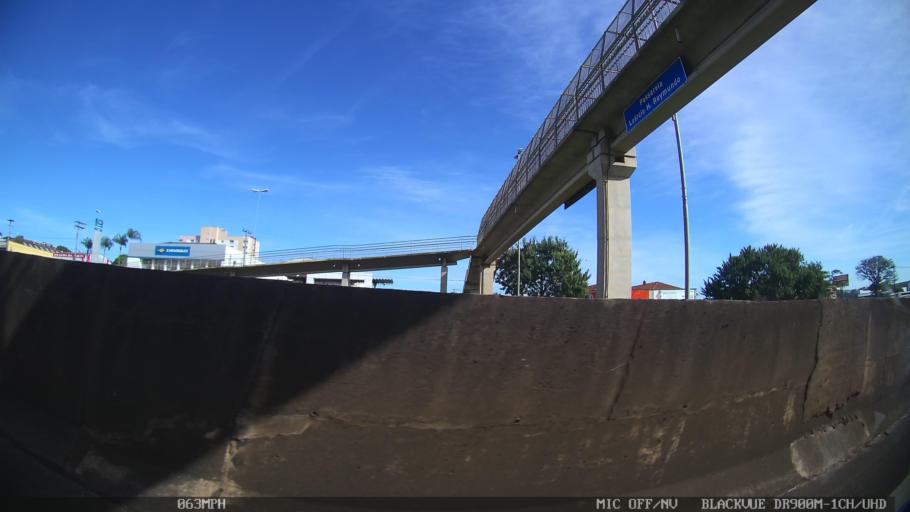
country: BR
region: Sao Paulo
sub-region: Araras
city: Araras
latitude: -22.3536
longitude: -47.3950
